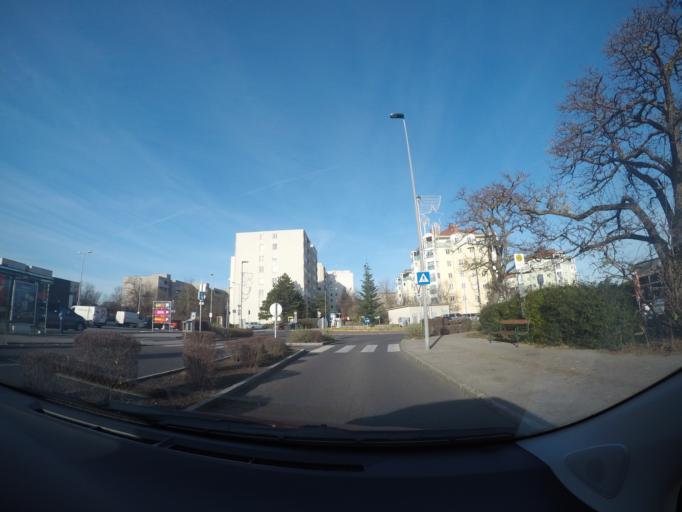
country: AT
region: Lower Austria
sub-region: Politischer Bezirk Modling
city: Wiener Neudorf
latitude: 48.0877
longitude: 16.3107
